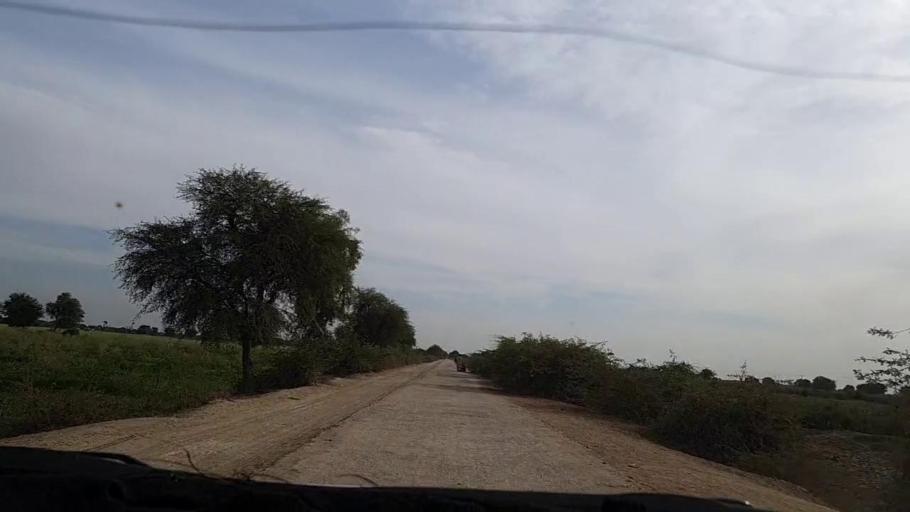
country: PK
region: Sindh
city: Dhoro Naro
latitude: 25.4275
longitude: 69.5217
